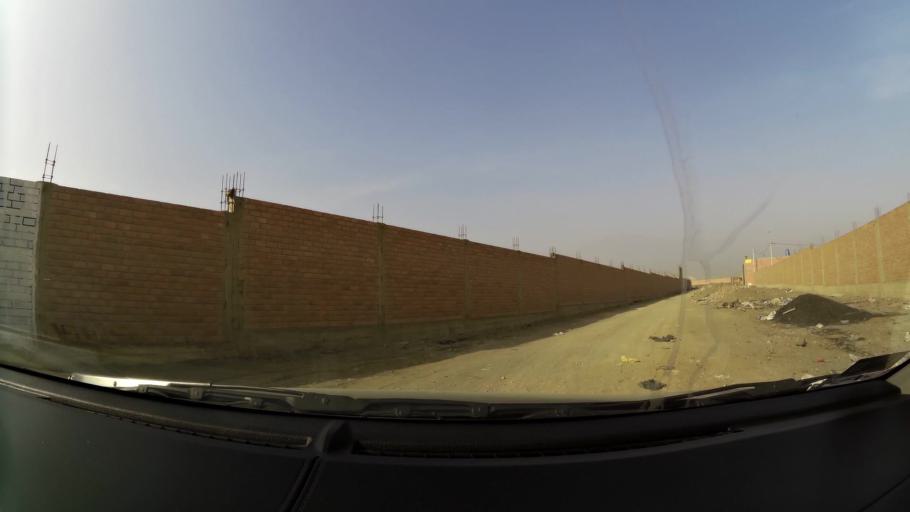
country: PE
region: Lima
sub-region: Lima
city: Santa Rosa
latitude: -11.7512
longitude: -77.1610
